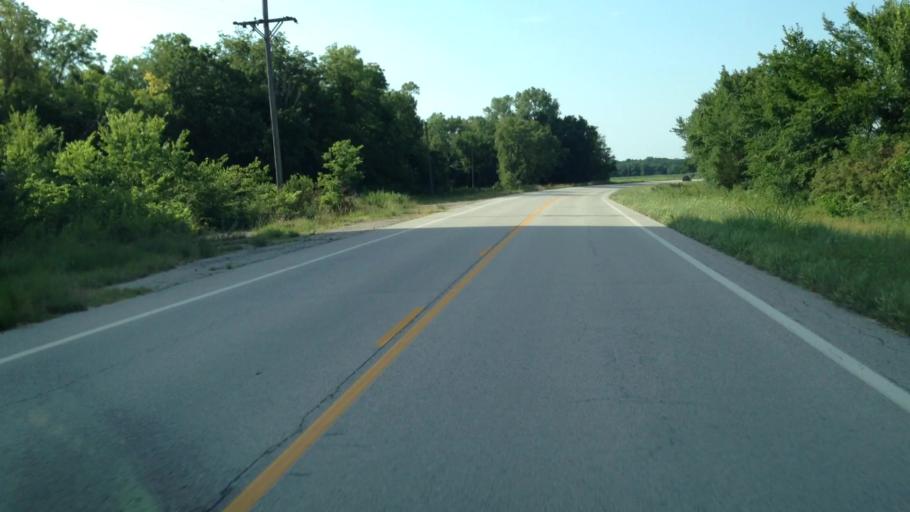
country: US
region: Kansas
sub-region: Allen County
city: Iola
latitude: 38.0283
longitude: -95.1733
